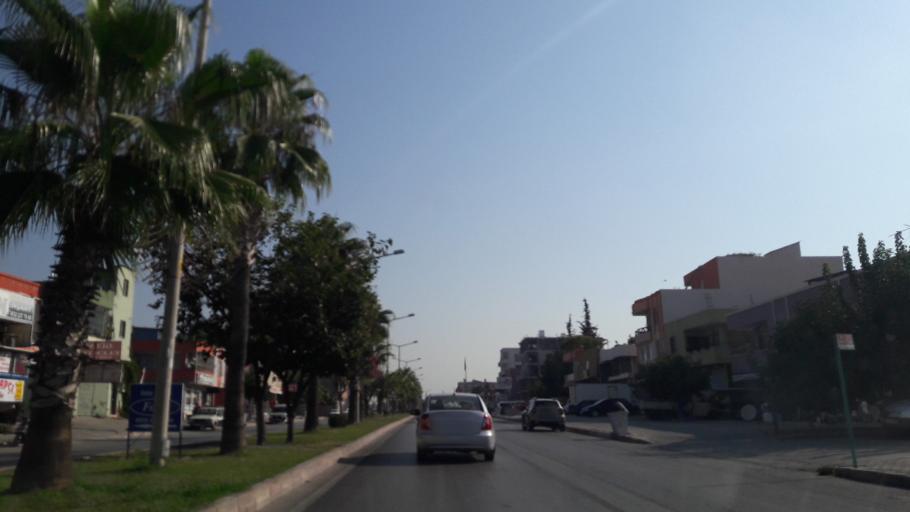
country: TR
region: Adana
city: Yuregir
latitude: 37.0391
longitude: 35.4248
